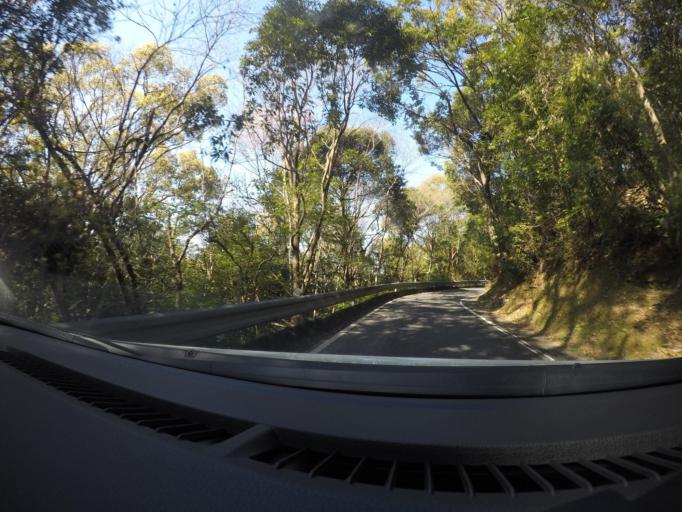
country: JP
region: Kochi
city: Kochi-shi
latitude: 33.5493
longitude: 133.5736
